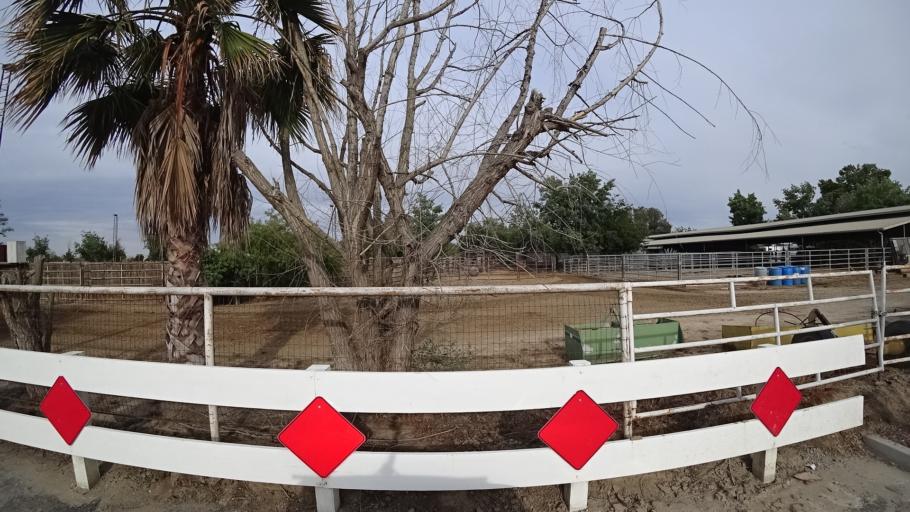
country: US
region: California
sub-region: Kings County
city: Armona
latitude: 36.3413
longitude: -119.6850
